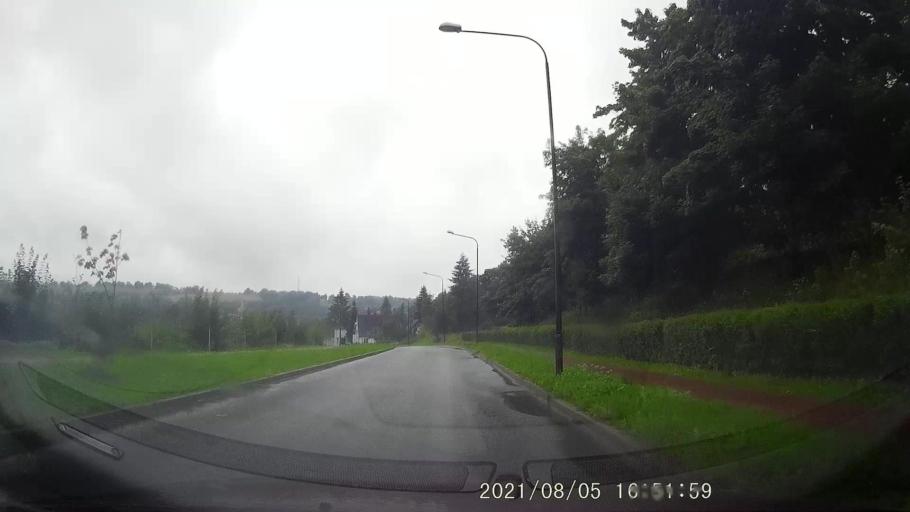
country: PL
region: Lower Silesian Voivodeship
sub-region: Powiat klodzki
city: Duszniki-Zdroj
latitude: 50.3982
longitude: 16.3911
